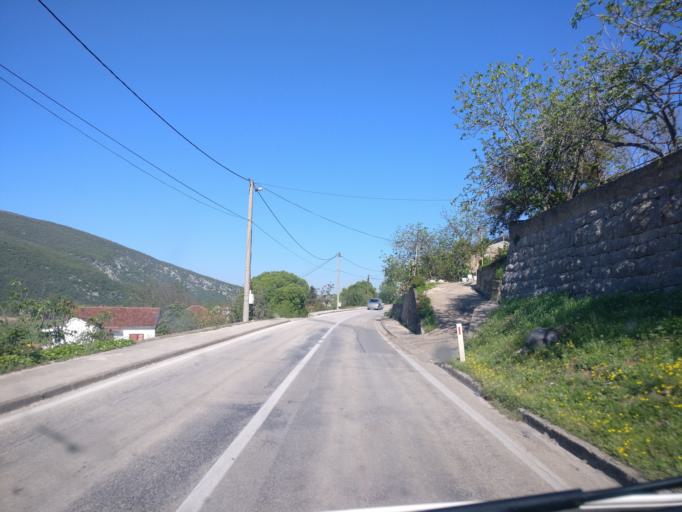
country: BA
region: Federation of Bosnia and Herzegovina
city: Capljina
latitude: 43.1358
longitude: 17.6731
